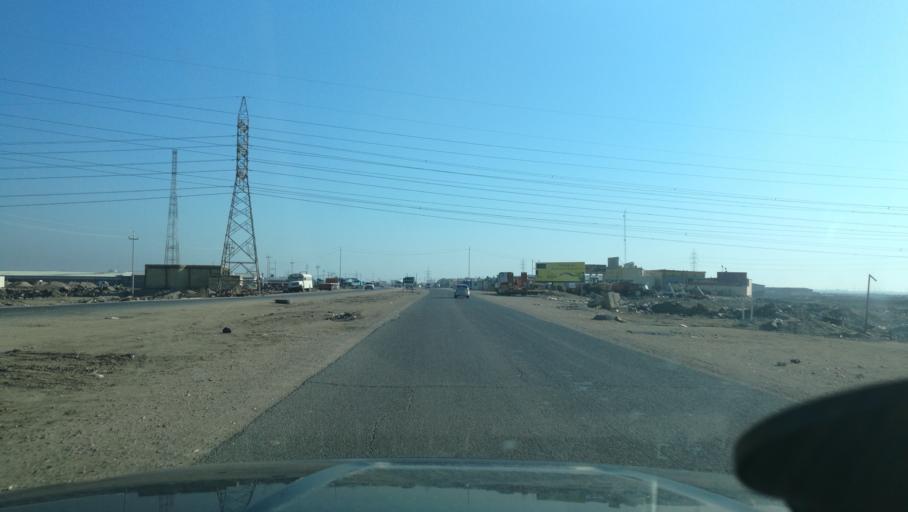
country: IQ
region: Dhi Qar
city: An Nasiriyah
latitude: 30.9985
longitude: 46.2539
